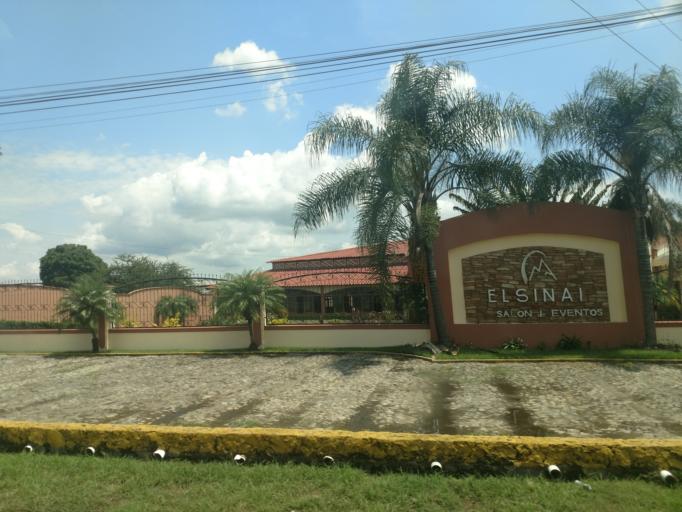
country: MX
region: Nayarit
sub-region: Tepic
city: La Corregidora
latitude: 21.4674
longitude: -104.8348
